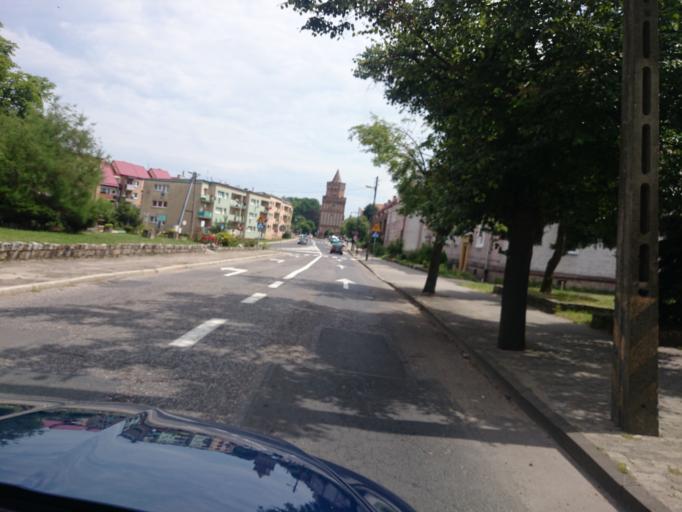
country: PL
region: West Pomeranian Voivodeship
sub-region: Powiat gryfinski
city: Chojna
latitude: 52.9620
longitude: 14.4300
